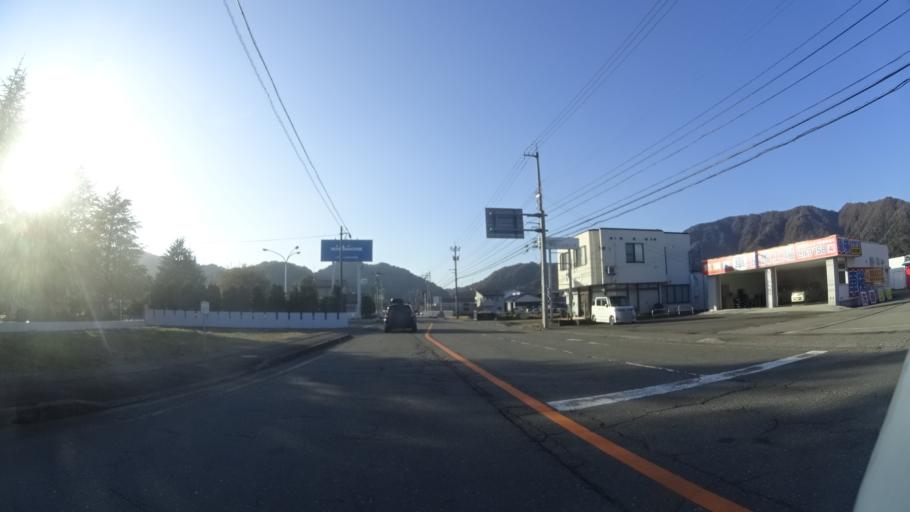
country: JP
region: Fukui
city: Ono
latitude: 35.9926
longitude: 136.4741
